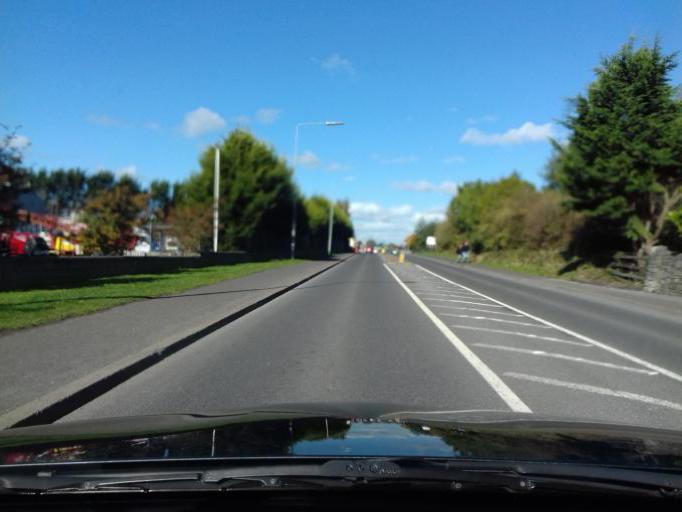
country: IE
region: Leinster
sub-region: An Mhi
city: Ashbourne
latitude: 53.5193
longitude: -6.4093
